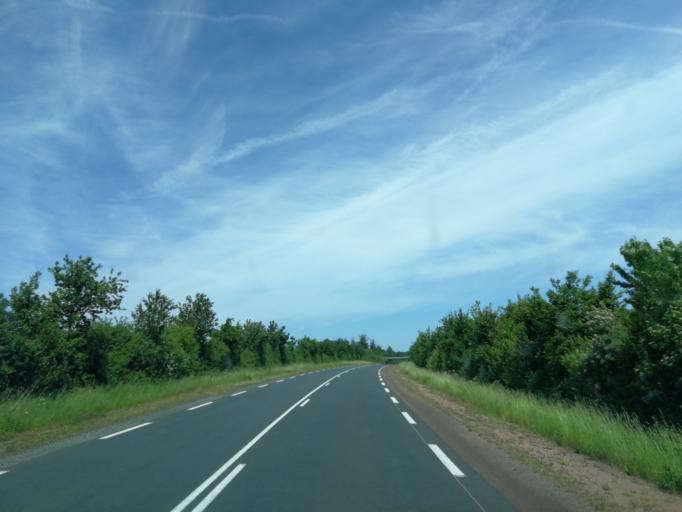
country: FR
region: Pays de la Loire
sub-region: Departement de la Vendee
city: Pissotte
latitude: 46.5070
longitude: -0.8180
